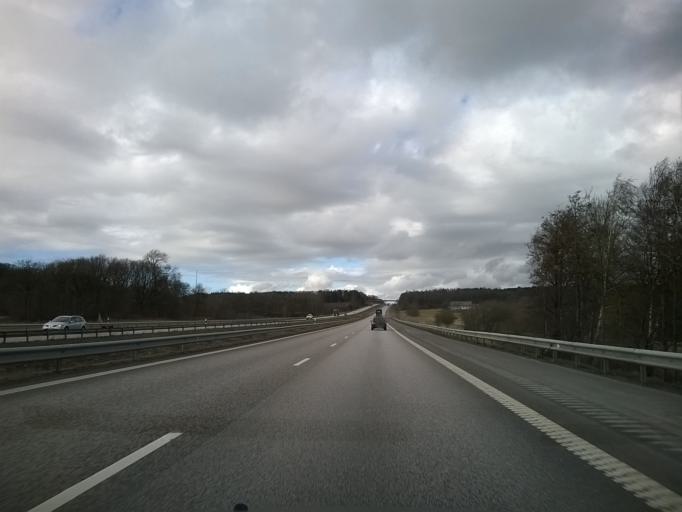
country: SE
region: Halland
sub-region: Kungsbacka Kommun
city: Frillesas
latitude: 57.2608
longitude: 12.2163
